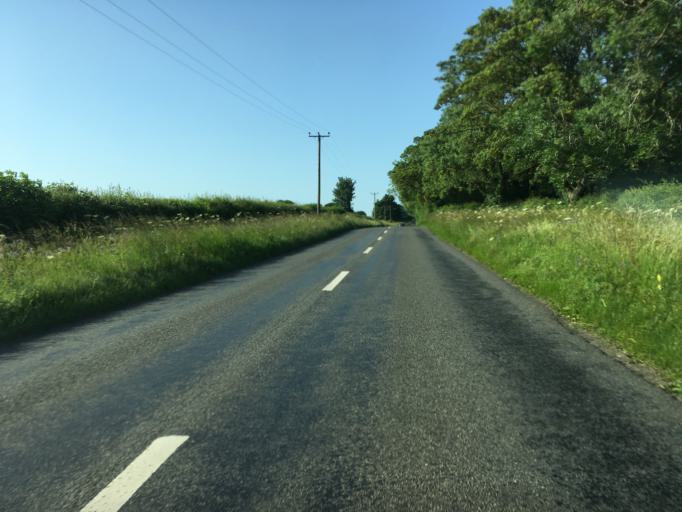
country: GB
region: England
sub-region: Oxfordshire
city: Charlbury
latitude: 51.8998
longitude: -1.4674
